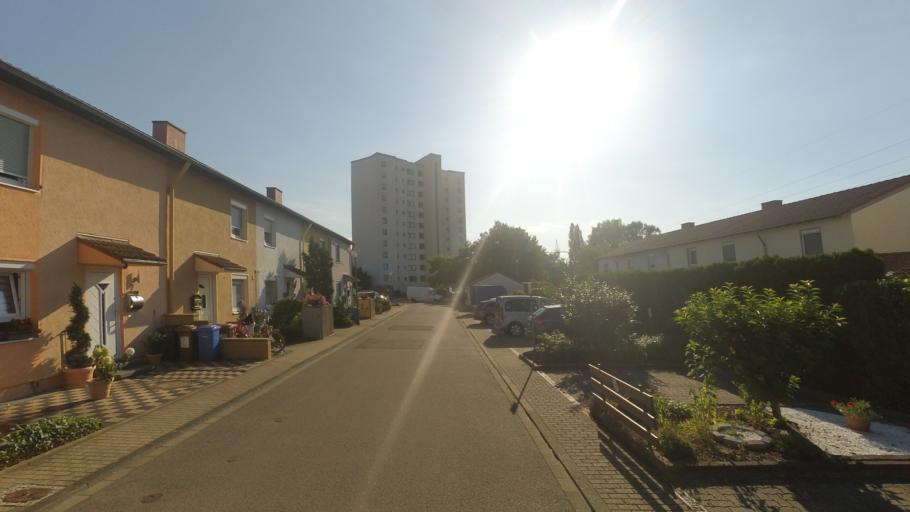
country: DE
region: Rheinland-Pfalz
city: Gartenstadt
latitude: 49.4671
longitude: 8.4022
